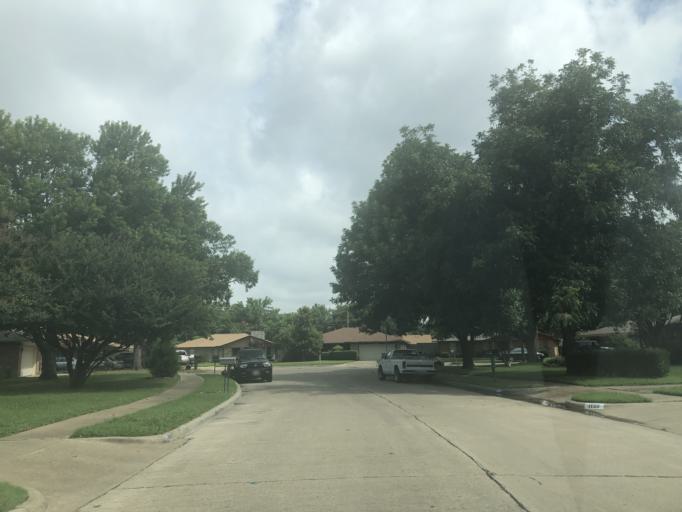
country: US
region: Texas
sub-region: Dallas County
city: Irving
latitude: 32.8019
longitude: -96.9721
